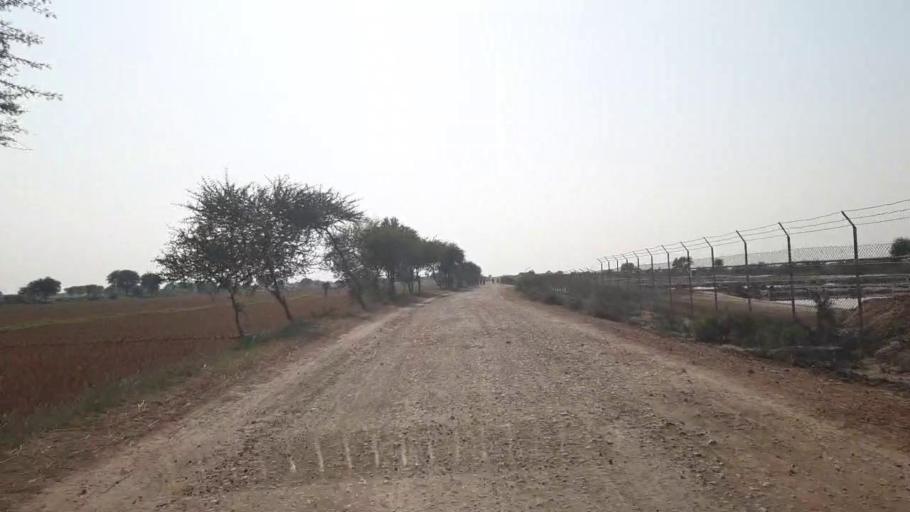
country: PK
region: Sindh
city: Matli
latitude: 24.9432
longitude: 68.6805
